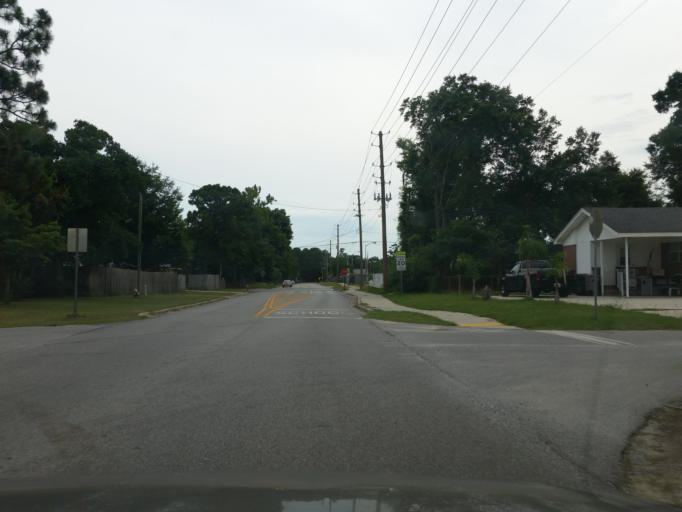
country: US
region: Florida
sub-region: Escambia County
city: Ferry Pass
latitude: 30.4893
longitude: -87.2052
